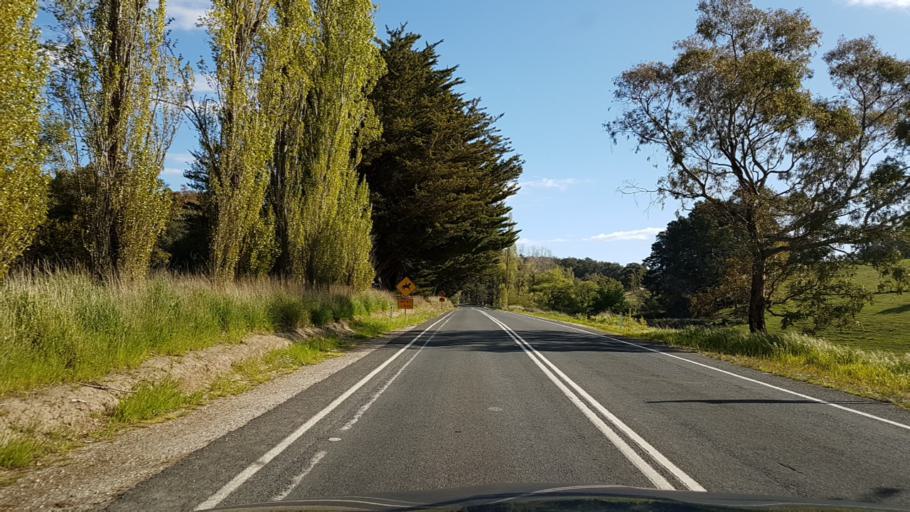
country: AU
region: South Australia
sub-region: Adelaide Hills
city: Gumeracha
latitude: -34.8649
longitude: 138.8893
